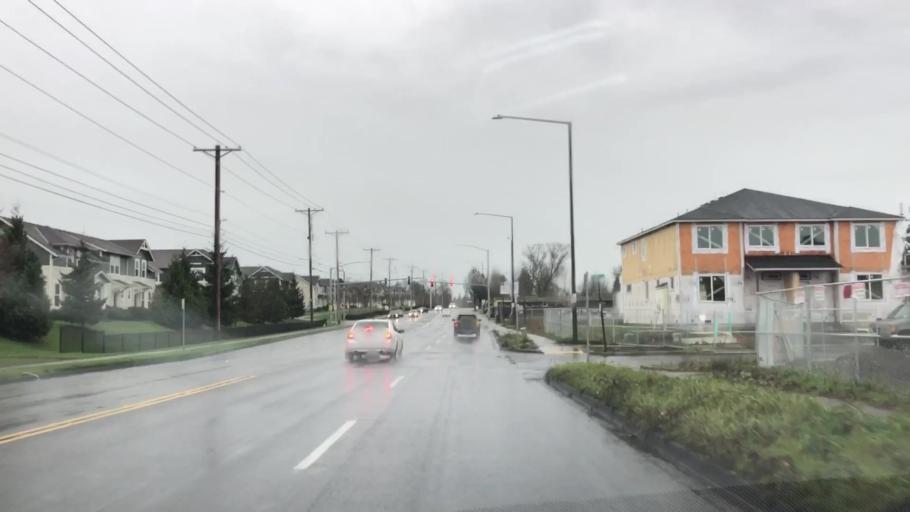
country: US
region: Washington
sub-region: Pierce County
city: Waller
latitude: 47.2129
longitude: -122.4082
